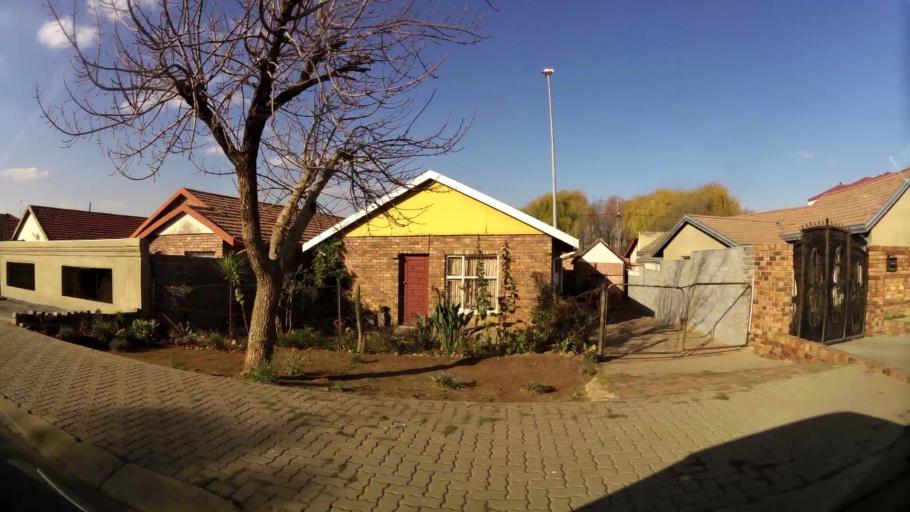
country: ZA
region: Gauteng
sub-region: City of Johannesburg Metropolitan Municipality
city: Soweto
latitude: -26.2771
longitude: 27.9106
